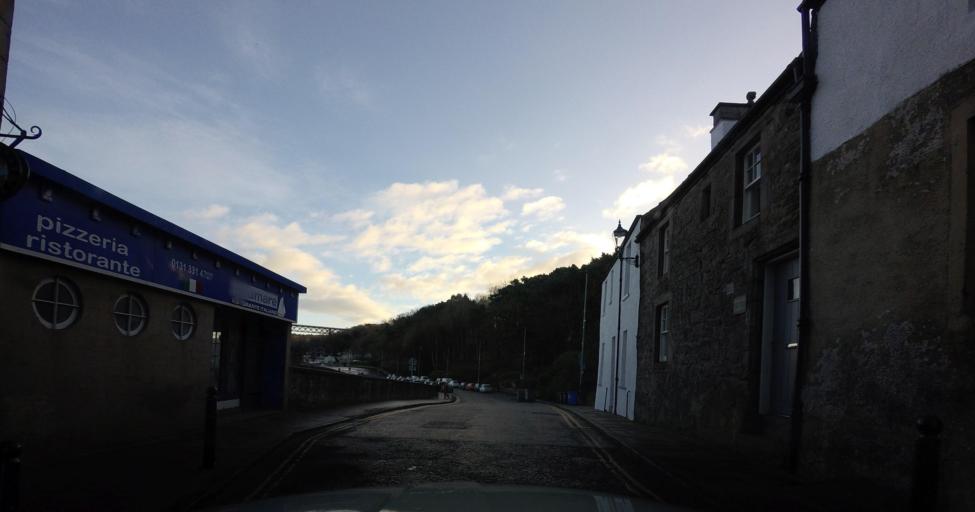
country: GB
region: Scotland
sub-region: Edinburgh
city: Queensferry
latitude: 55.9899
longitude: -3.3929
